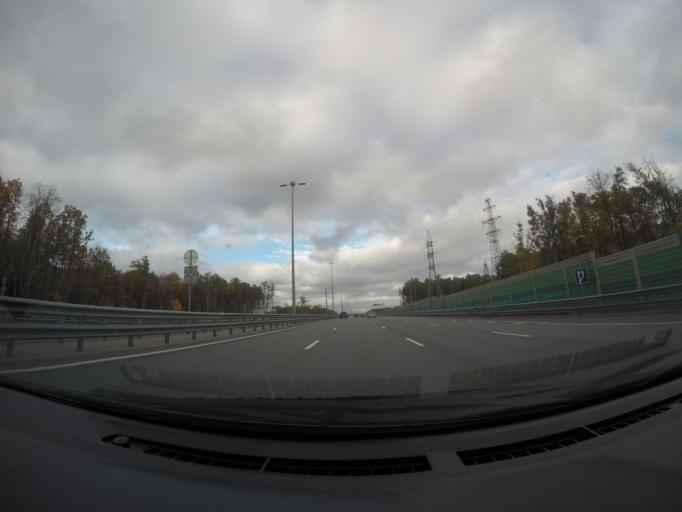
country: RU
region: Moskovskaya
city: Odintsovo
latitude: 55.7076
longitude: 37.3099
